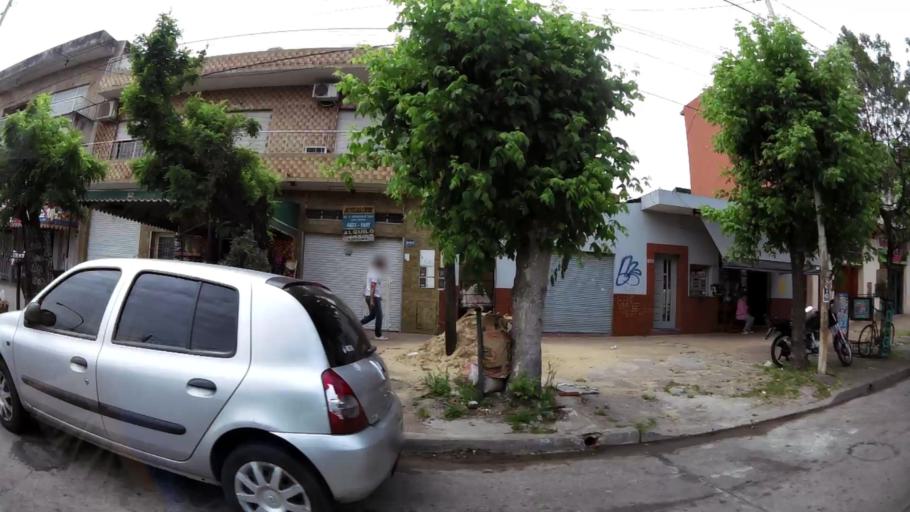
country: AR
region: Buenos Aires F.D.
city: Villa Lugano
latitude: -34.6877
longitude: -58.4953
